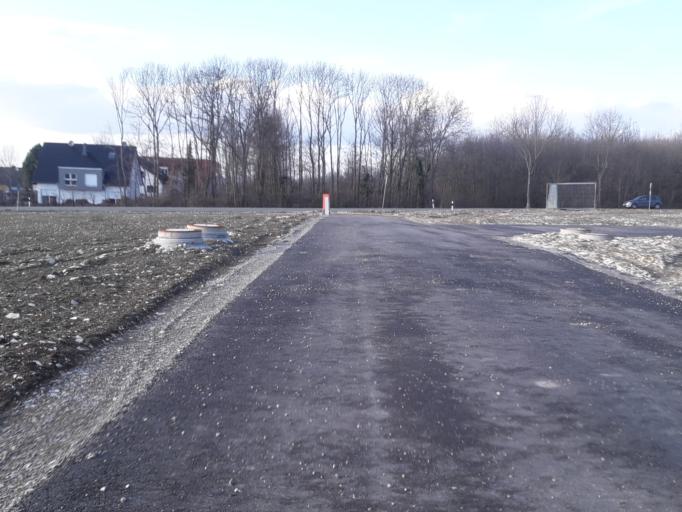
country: DE
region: North Rhine-Westphalia
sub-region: Regierungsbezirk Detmold
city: Paderborn
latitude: 51.7185
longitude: 8.8106
